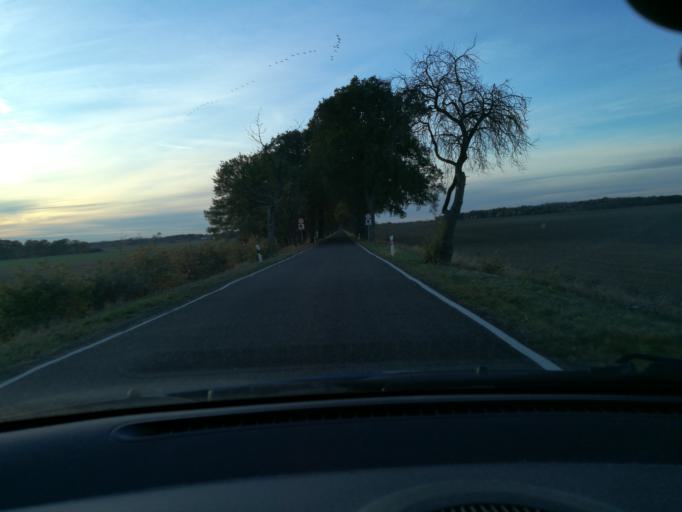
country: DE
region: Brandenburg
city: Karstadt
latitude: 53.0946
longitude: 11.7207
